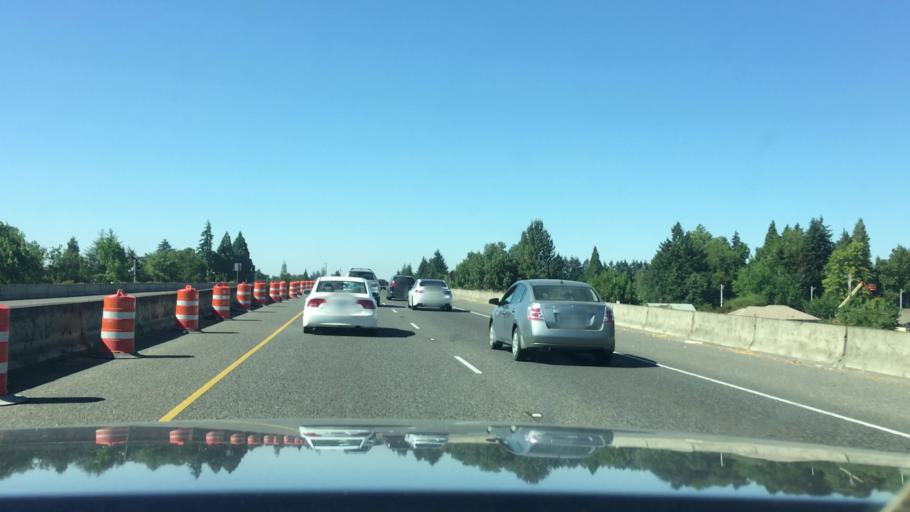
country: US
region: Oregon
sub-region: Lane County
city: Eugene
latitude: 44.0685
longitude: -123.1737
